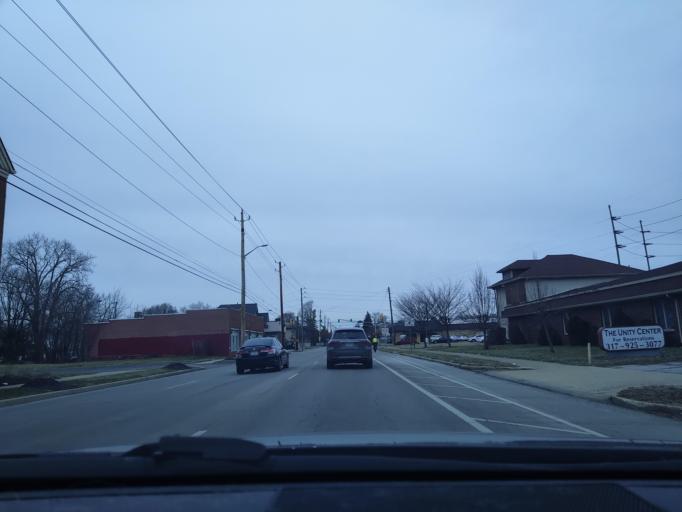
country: US
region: Indiana
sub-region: Marion County
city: Indianapolis
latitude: 39.7963
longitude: -86.1591
